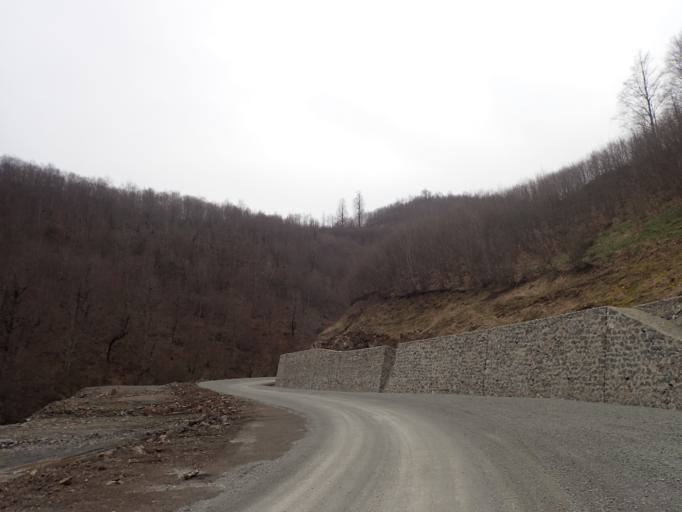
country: TR
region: Ordu
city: Kumru
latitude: 40.8024
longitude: 37.1815
